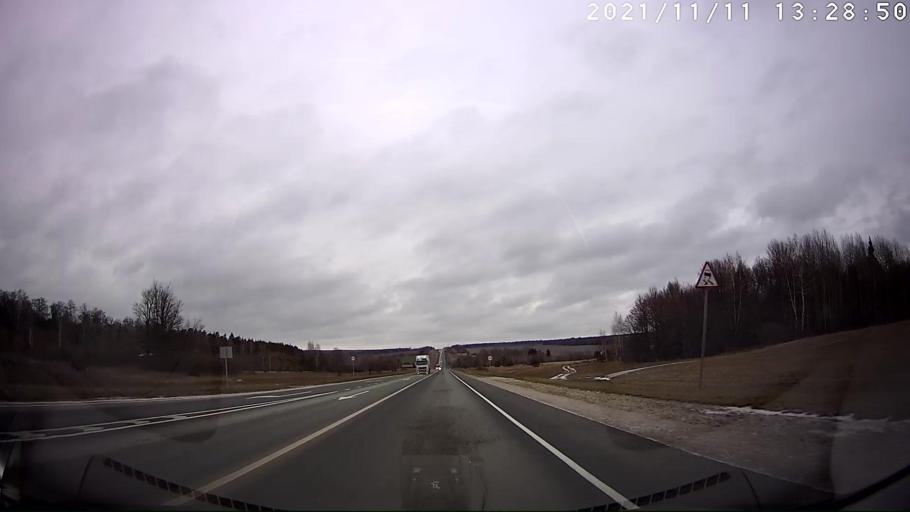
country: RU
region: Chuvashia
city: Komsomol'skoye
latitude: 55.3000
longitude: 47.5555
